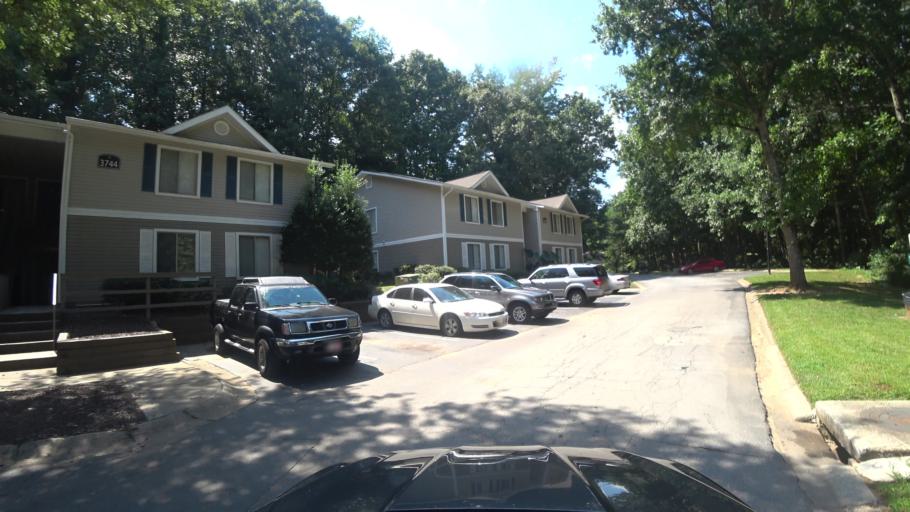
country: US
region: Georgia
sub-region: Gwinnett County
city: Norcross
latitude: 33.9546
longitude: -84.2531
